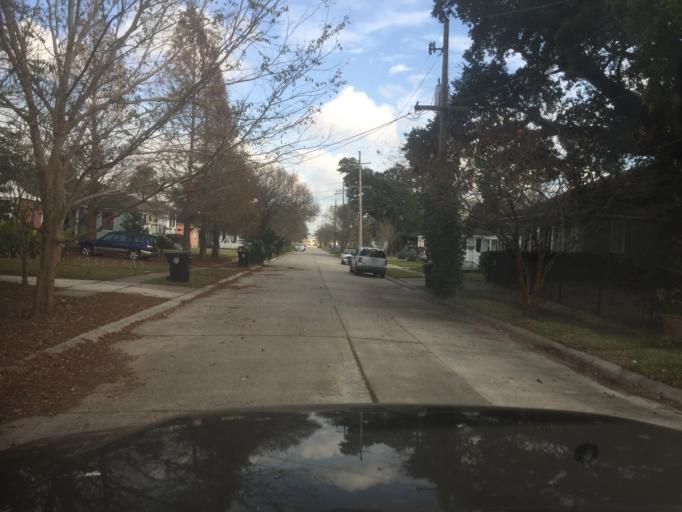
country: US
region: Louisiana
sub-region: Orleans Parish
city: New Orleans
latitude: 29.9900
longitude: -90.0858
